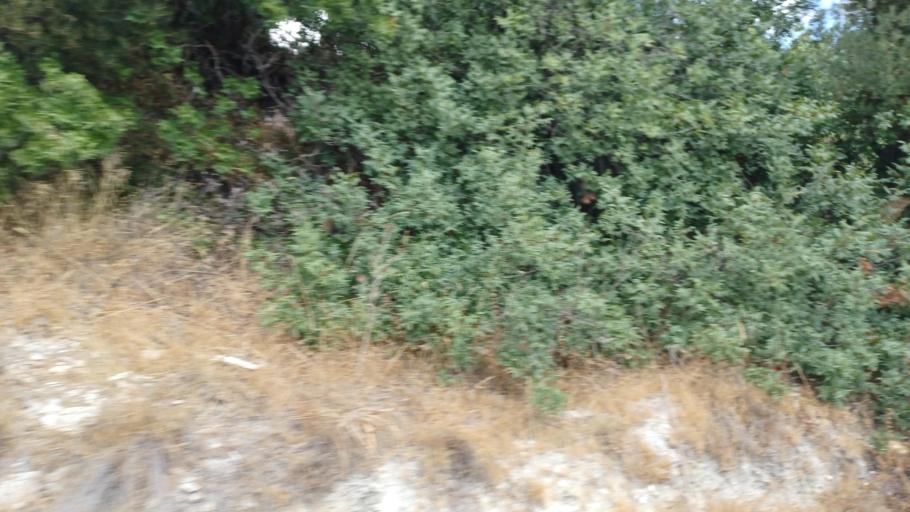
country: CY
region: Limassol
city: Pachna
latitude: 34.7996
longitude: 32.6647
